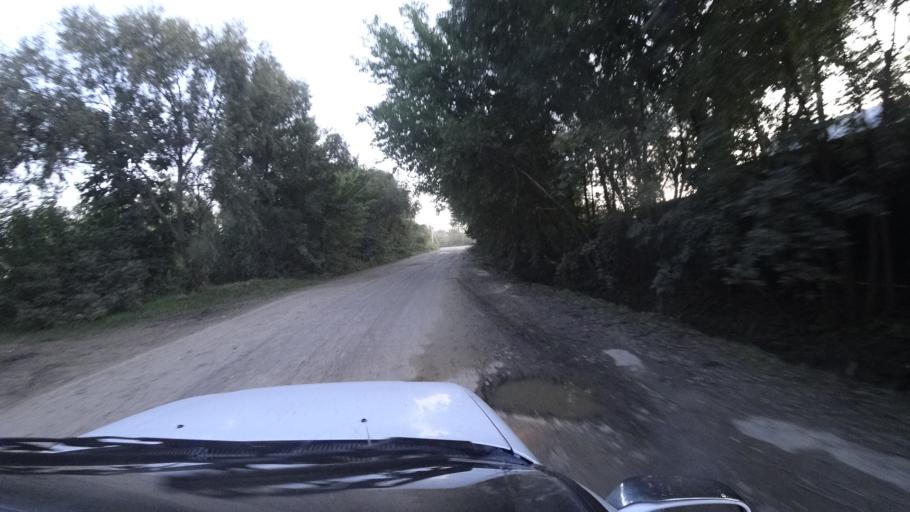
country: RU
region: Primorskiy
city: Dal'nerechensk
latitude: 45.9351
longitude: 133.7587
